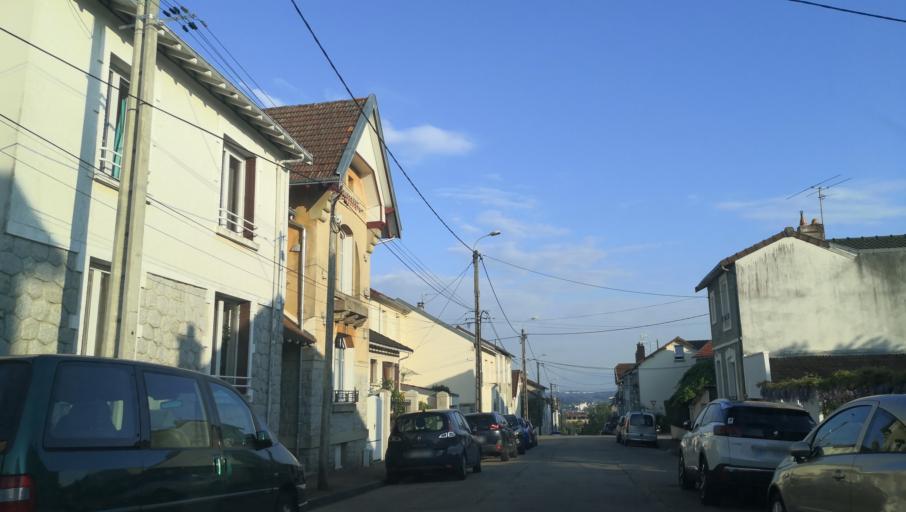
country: FR
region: Limousin
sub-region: Departement de la Haute-Vienne
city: Limoges
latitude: 45.8479
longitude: 1.2513
